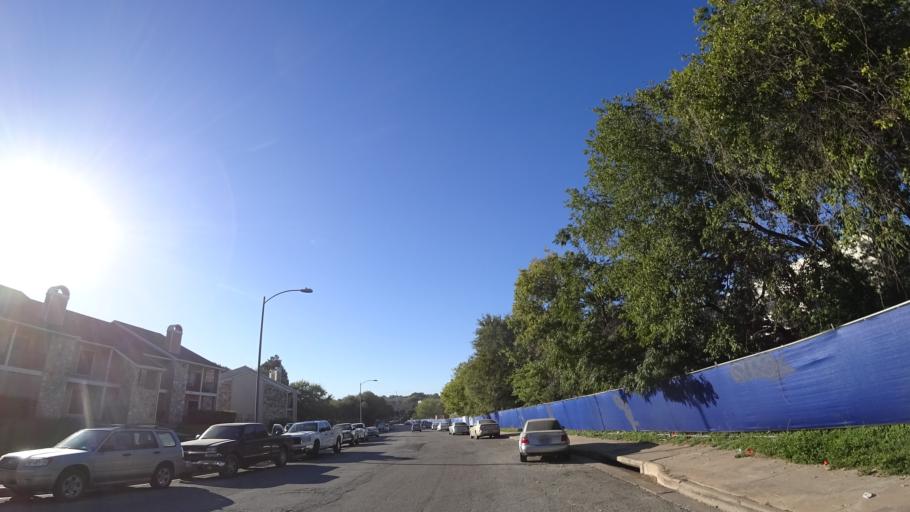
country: US
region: Texas
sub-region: Travis County
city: Austin
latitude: 30.2297
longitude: -97.7193
